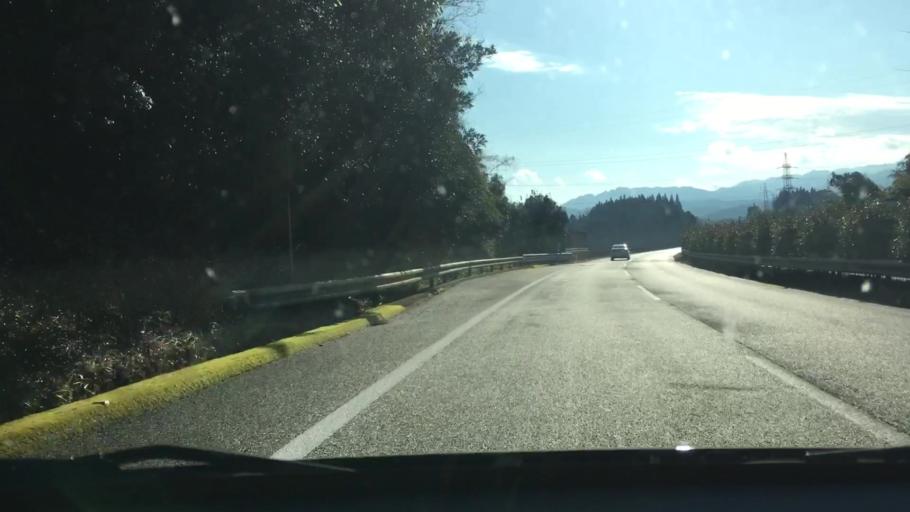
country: JP
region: Kumamoto
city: Hitoyoshi
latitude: 32.2161
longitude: 130.7792
